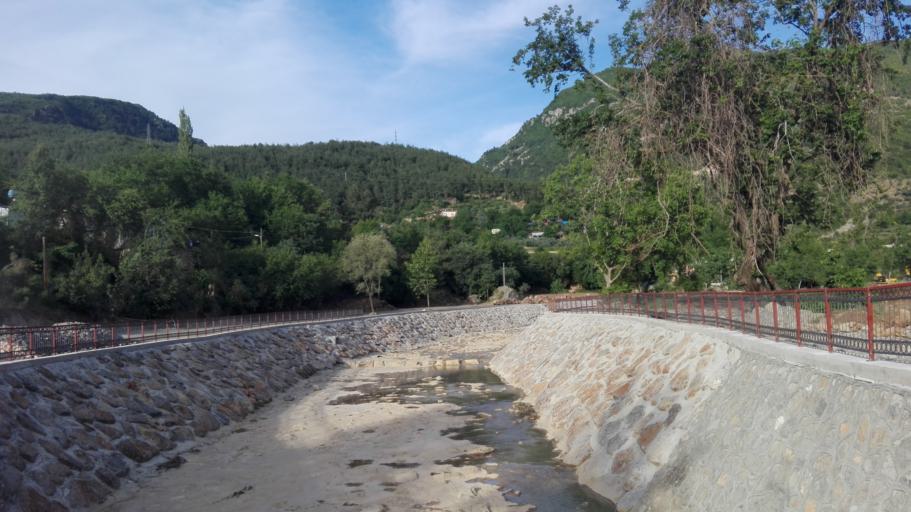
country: TR
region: Osmaniye
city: Haruniye
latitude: 37.2812
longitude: 36.4658
